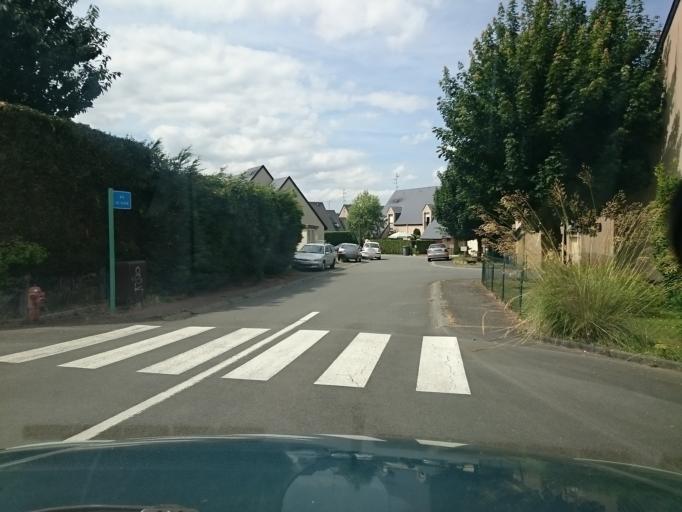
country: FR
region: Lower Normandy
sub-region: Departement du Calvados
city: Ifs
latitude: 49.1368
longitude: -0.3469
